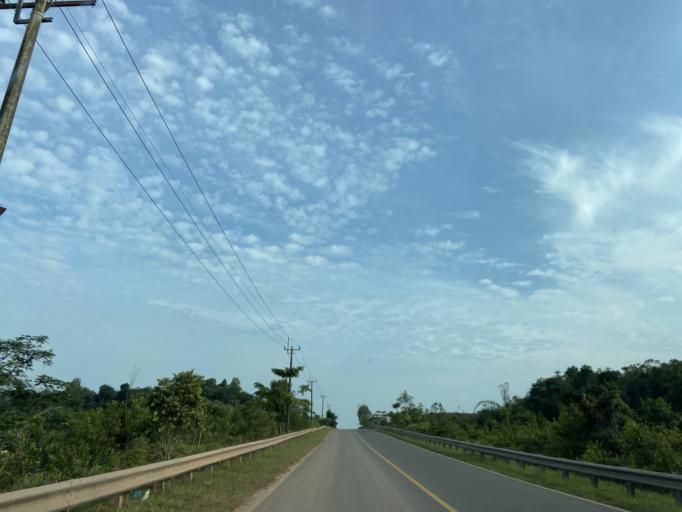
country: ID
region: Riau Islands
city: Tanjungpinang
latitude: 0.9130
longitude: 104.1213
